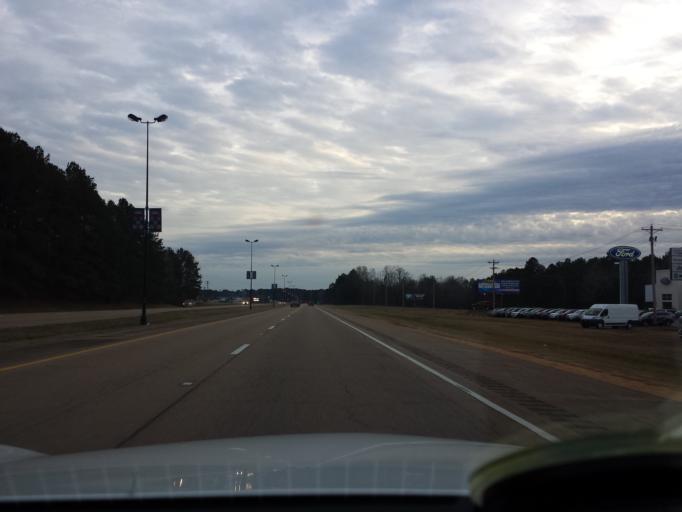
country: US
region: Mississippi
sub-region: Winston County
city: Louisville
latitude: 33.1332
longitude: -89.0869
